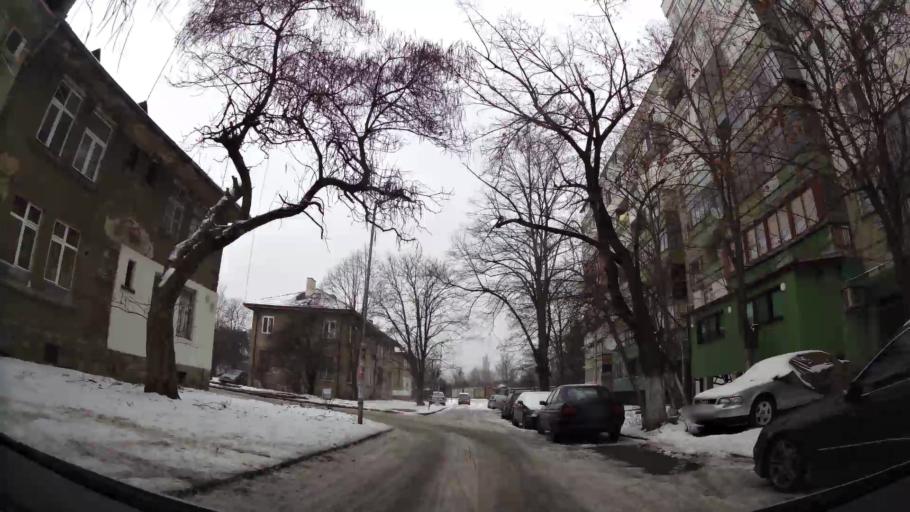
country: BG
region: Sofia-Capital
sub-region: Stolichna Obshtina
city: Sofia
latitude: 42.7157
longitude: 23.3040
